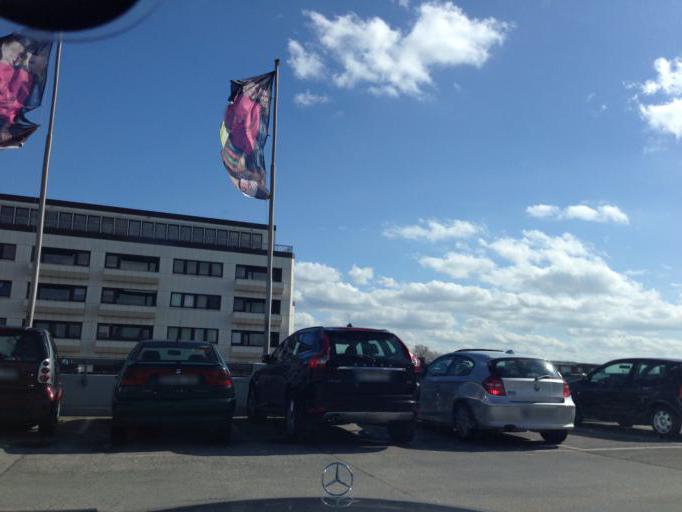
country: DE
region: Hamburg
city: Wandsbek
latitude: 53.5399
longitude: 10.1058
